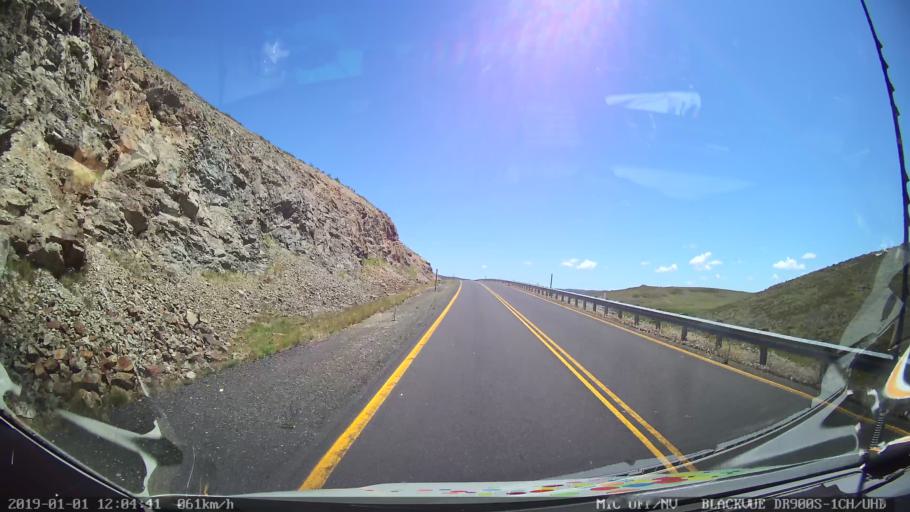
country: AU
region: New South Wales
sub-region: Snowy River
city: Jindabyne
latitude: -35.8648
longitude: 148.4964
